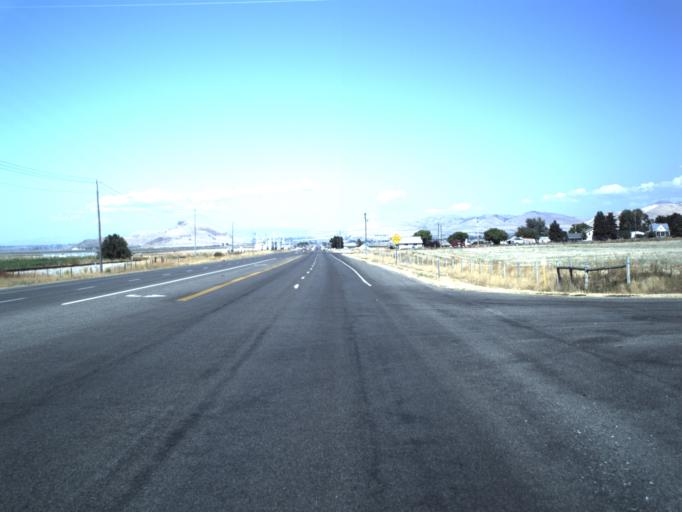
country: US
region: Utah
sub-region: Cache County
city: Richmond
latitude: 41.9589
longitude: -111.8128
